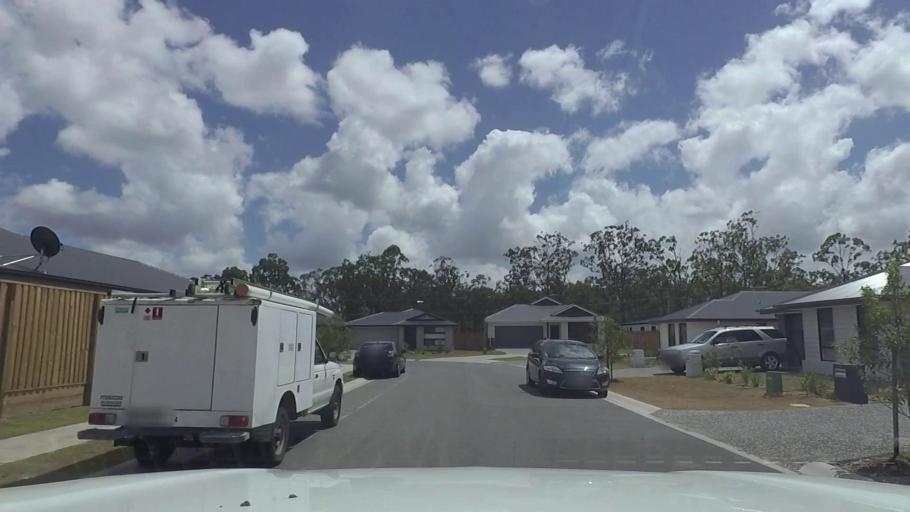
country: AU
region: Queensland
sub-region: Logan
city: Logan Reserve
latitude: -27.7079
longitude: 153.0808
